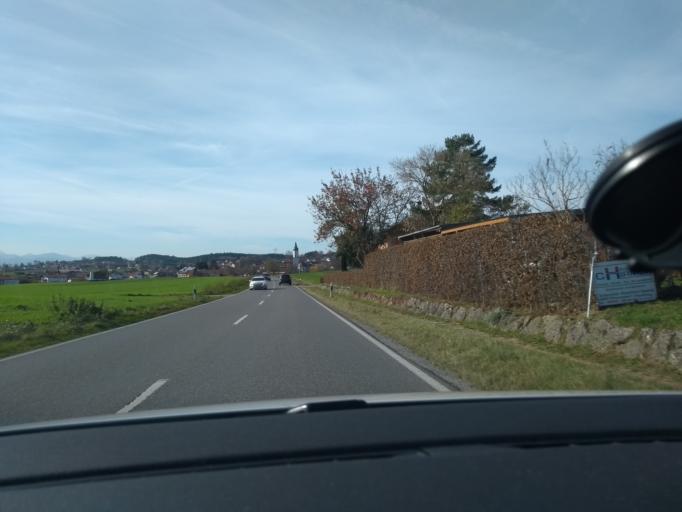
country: DE
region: Bavaria
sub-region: Upper Bavaria
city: Prutting
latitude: 47.8954
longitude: 12.2103
